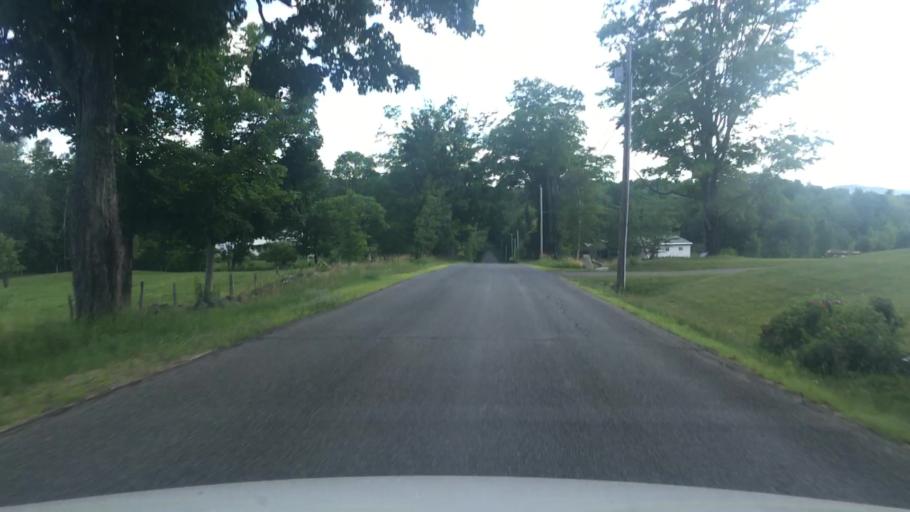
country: US
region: Maine
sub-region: Franklin County
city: Wilton
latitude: 44.6214
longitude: -70.2332
